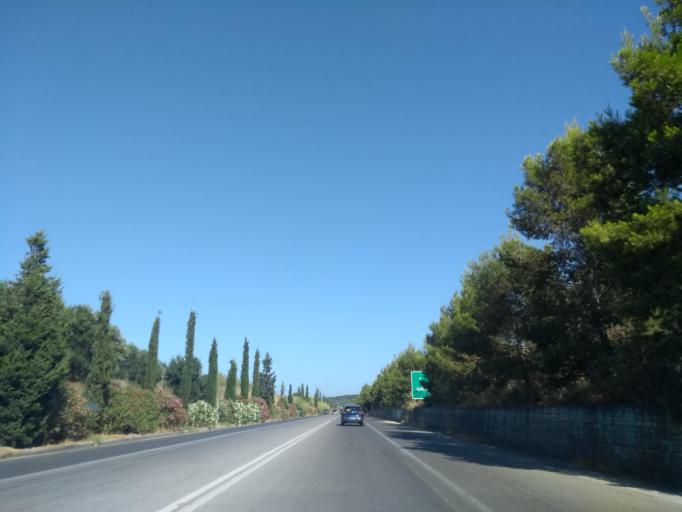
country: GR
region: Crete
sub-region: Nomos Chanias
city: Kolympari
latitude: 35.5282
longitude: 23.7937
